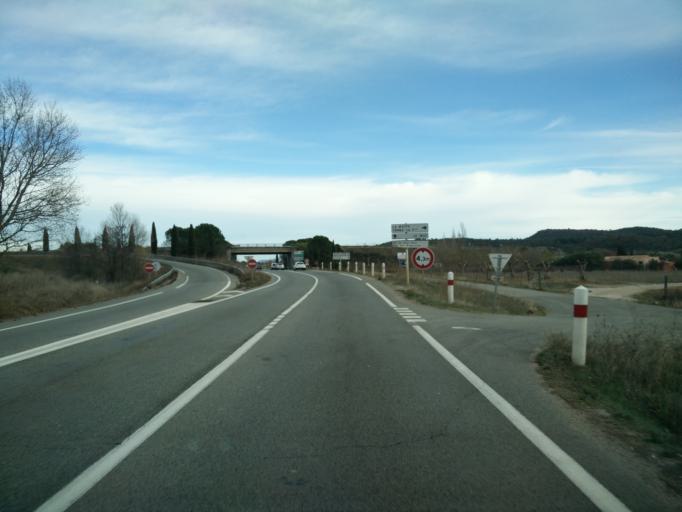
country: FR
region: Provence-Alpes-Cote d'Azur
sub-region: Departement du Var
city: Les Arcs
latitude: 43.4497
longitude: 6.4904
